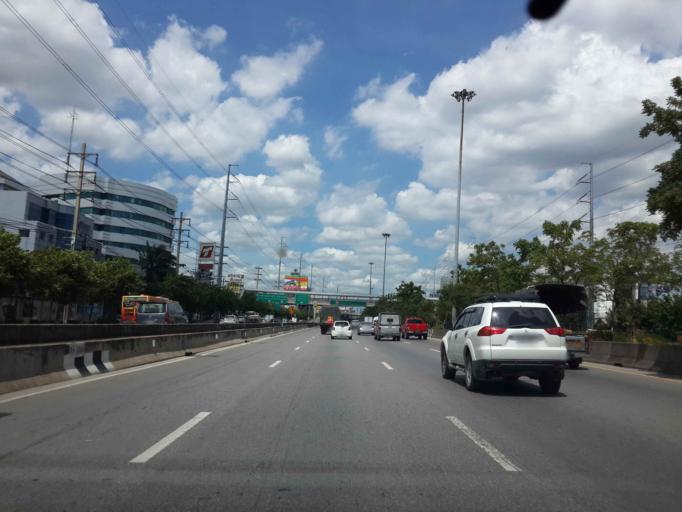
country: TH
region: Bangkok
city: Bang Khun Thian
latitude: 13.6550
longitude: 100.4274
